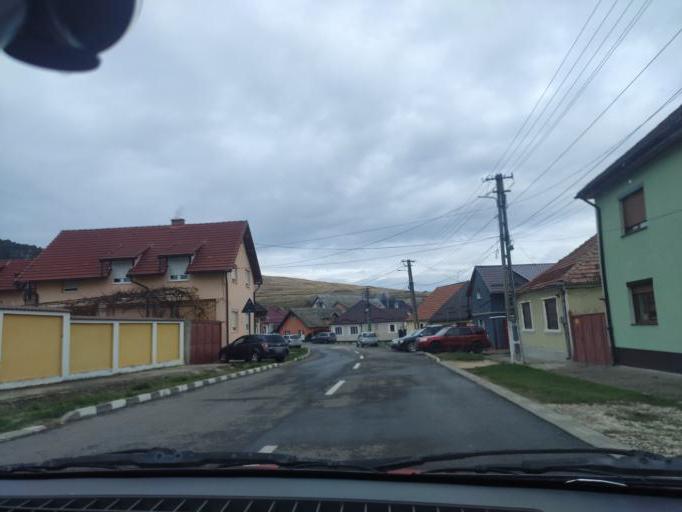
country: RO
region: Brasov
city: Codlea
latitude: 45.7050
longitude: 25.4461
